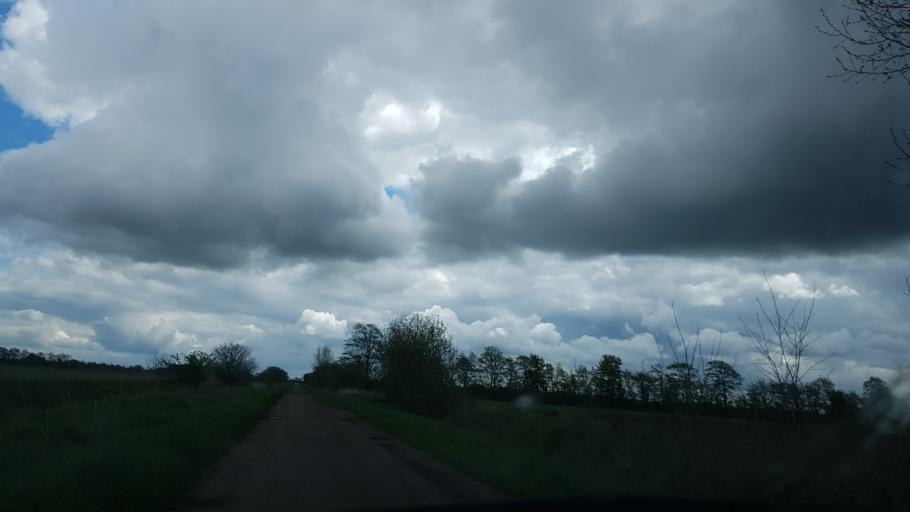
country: DK
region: South Denmark
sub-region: Haderslev Kommune
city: Vojens
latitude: 55.2357
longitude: 9.2036
